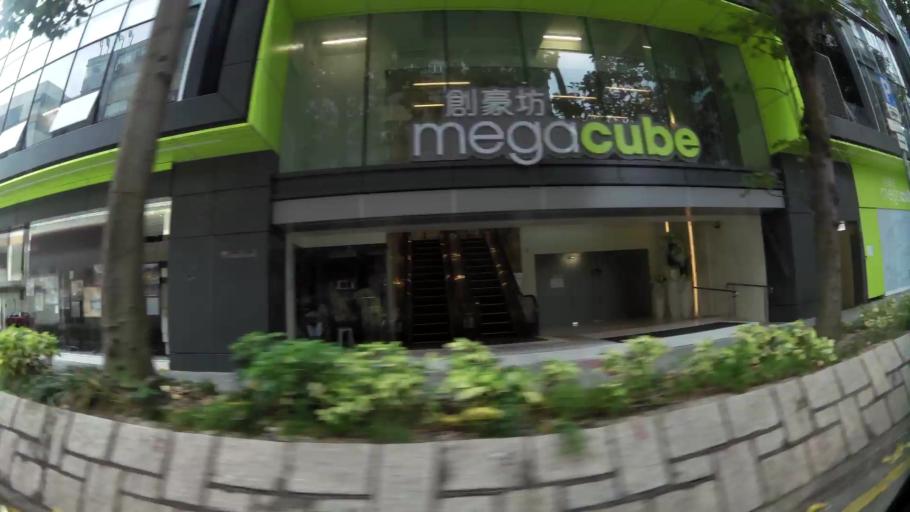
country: HK
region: Kowloon City
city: Kowloon
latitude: 22.3222
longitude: 114.2064
